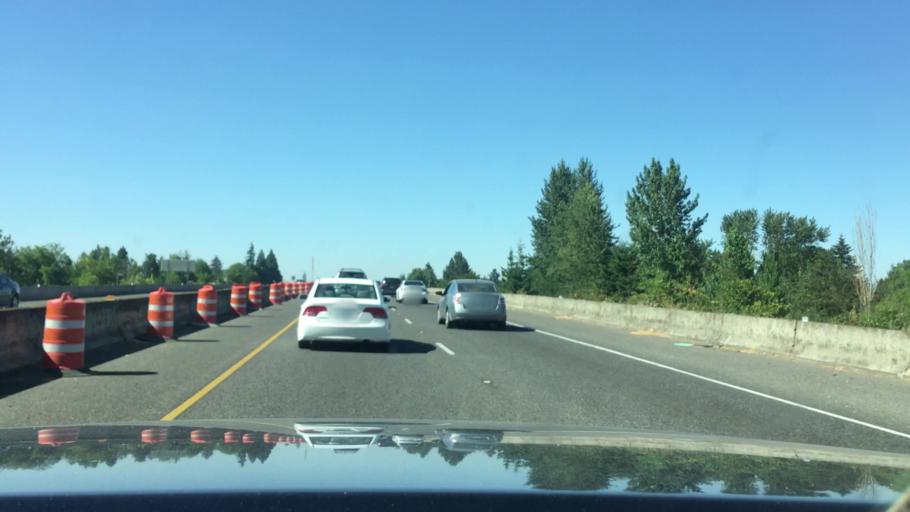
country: US
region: Oregon
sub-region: Lane County
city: Eugene
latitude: 44.0674
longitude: -123.1736
